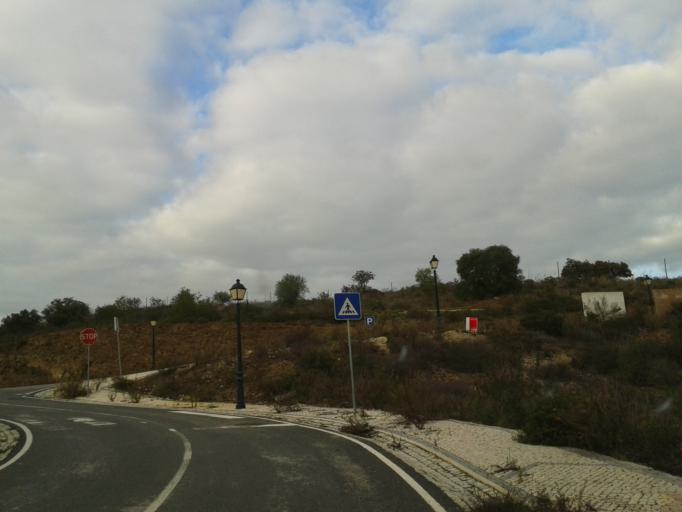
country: PT
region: Faro
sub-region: Castro Marim
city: Castro Marim
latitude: 37.2534
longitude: -7.4464
